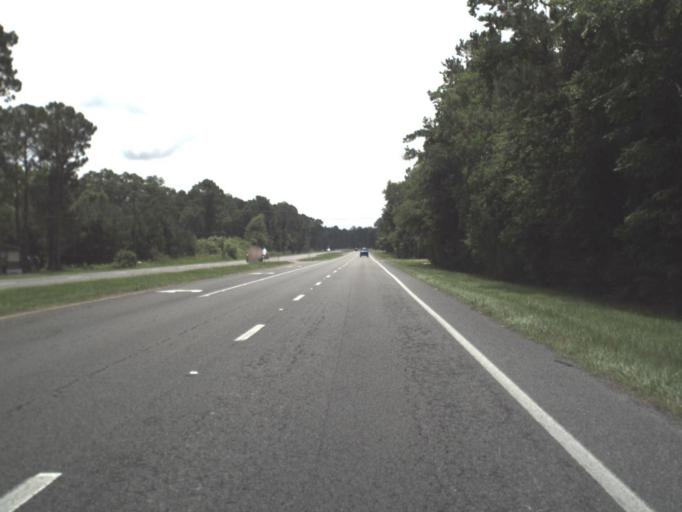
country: US
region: Florida
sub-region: Nassau County
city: Nassau Village-Ratliff
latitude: 30.5216
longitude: -81.7997
